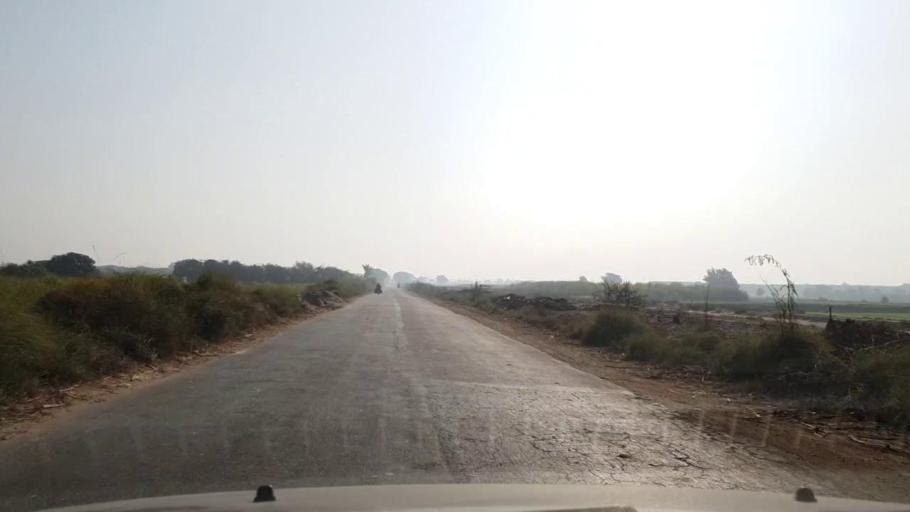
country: PK
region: Sindh
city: Matiari
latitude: 25.5878
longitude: 68.4816
